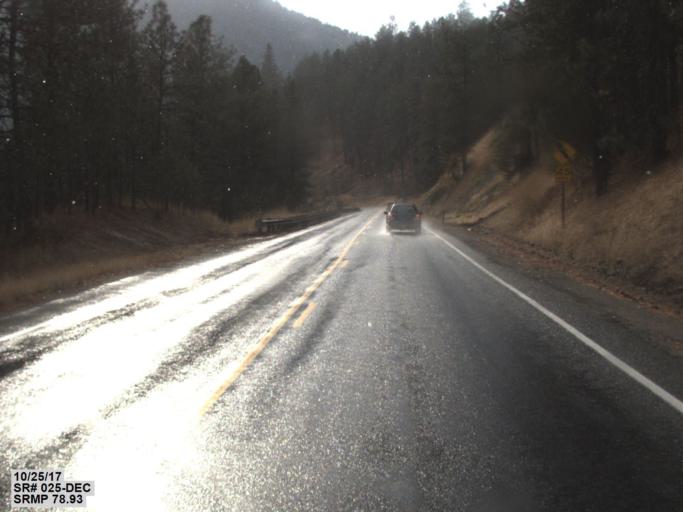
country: US
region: Washington
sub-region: Stevens County
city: Kettle Falls
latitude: 48.5785
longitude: -118.0807
